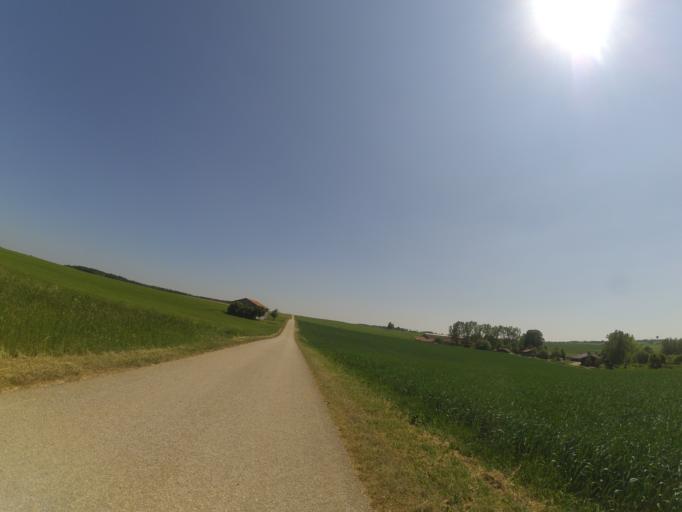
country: DE
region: Baden-Wuerttemberg
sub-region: Tuebingen Region
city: Merklingen
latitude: 48.5051
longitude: 9.7663
